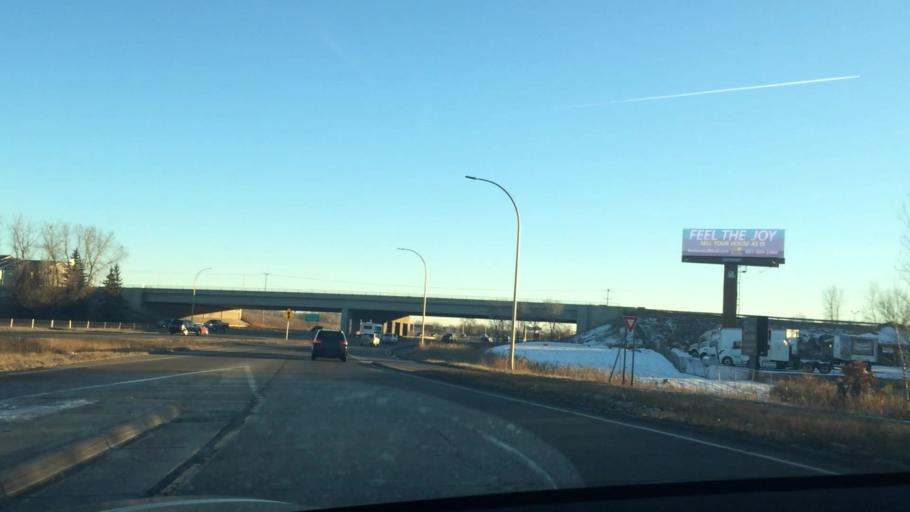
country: US
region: Minnesota
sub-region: Ramsey County
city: Mounds View
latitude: 45.1260
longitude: -93.1894
